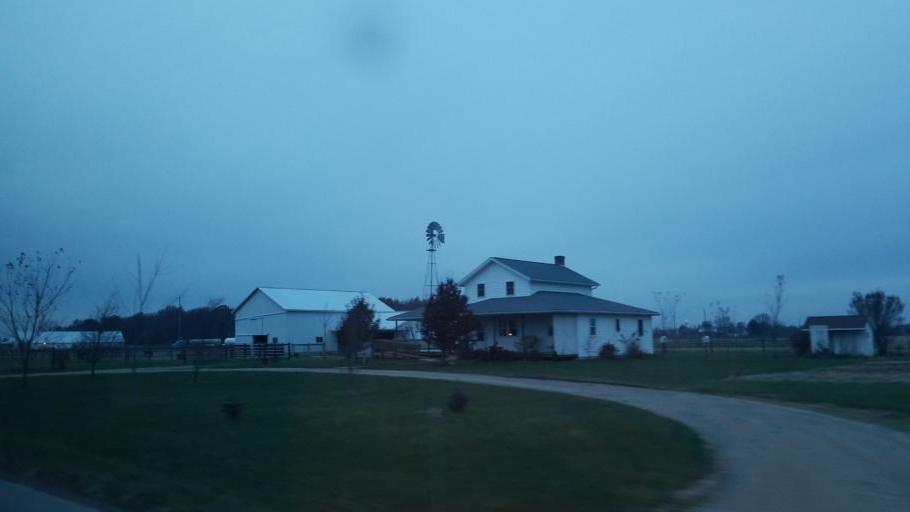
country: US
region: Indiana
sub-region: Adams County
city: Berne
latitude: 40.7315
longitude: -84.9377
